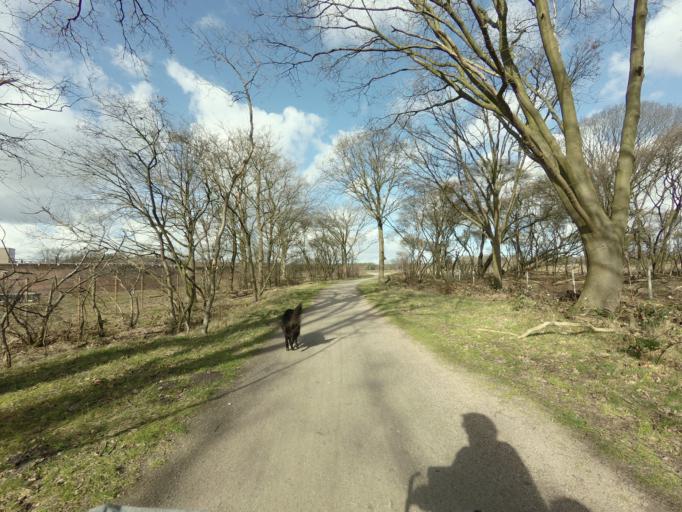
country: NL
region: North Holland
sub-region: Gemeente Hilversum
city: Hilversum
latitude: 52.2246
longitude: 5.2104
